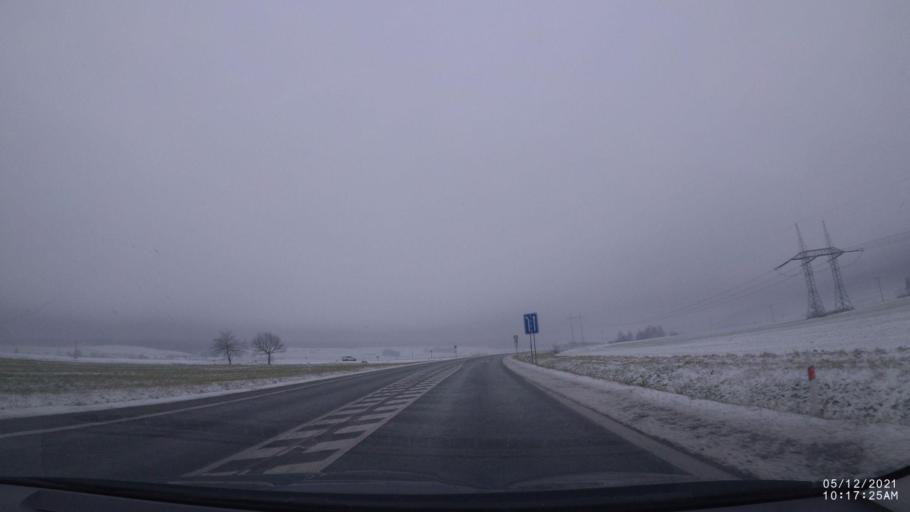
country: CZ
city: Vamberk
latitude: 50.1079
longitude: 16.2902
